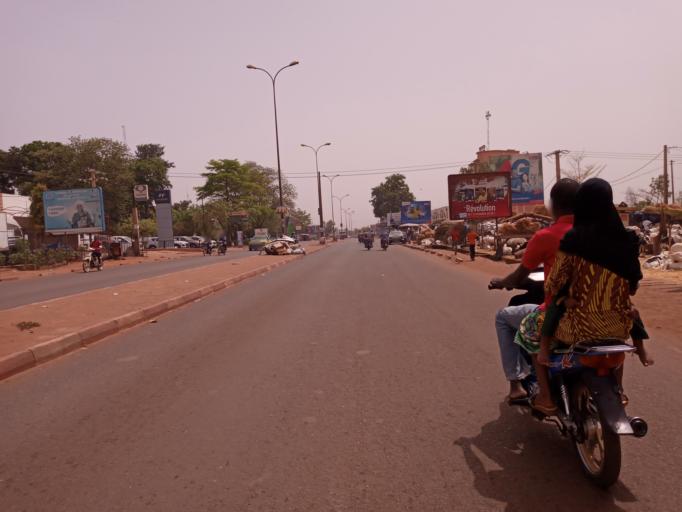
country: ML
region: Bamako
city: Bamako
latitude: 12.6583
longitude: -7.9649
